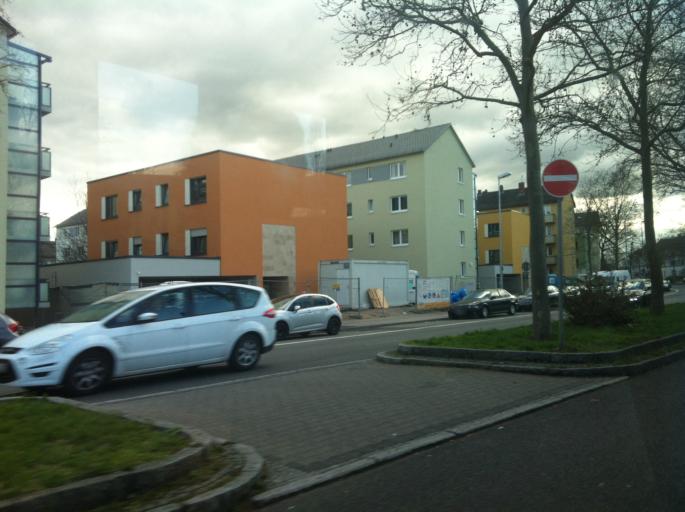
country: DE
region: Rheinland-Pfalz
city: Mainz
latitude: 50.0077
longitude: 8.2925
